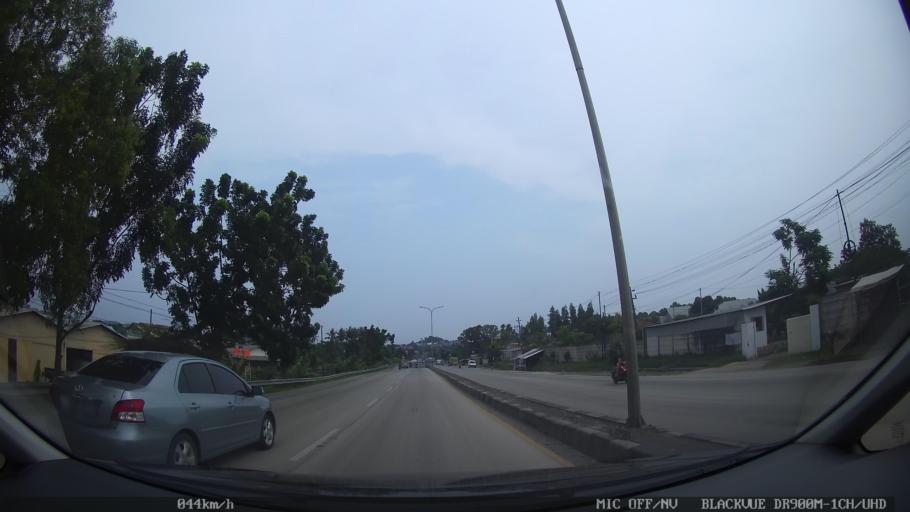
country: ID
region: Lampung
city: Bandarlampung
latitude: -5.4137
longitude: 105.2953
